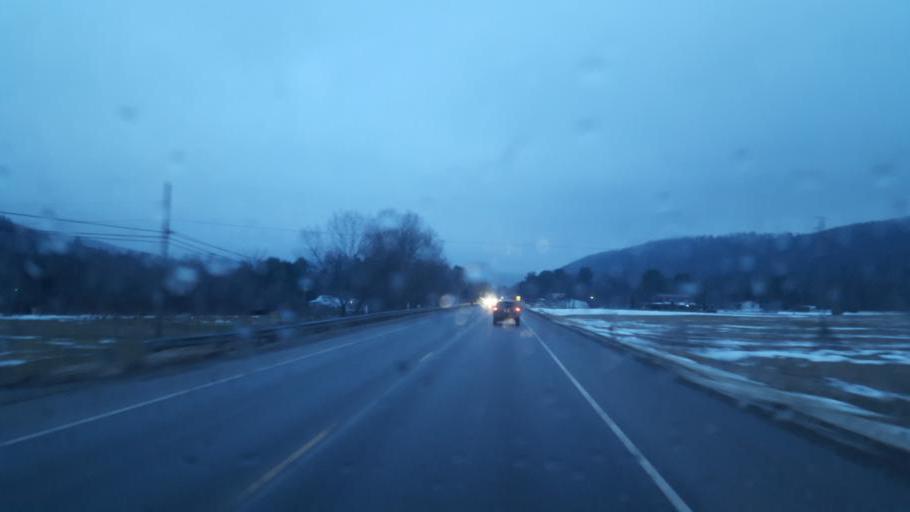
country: US
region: Pennsylvania
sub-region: McKean County
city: Port Allegany
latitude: 41.7943
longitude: -78.2490
